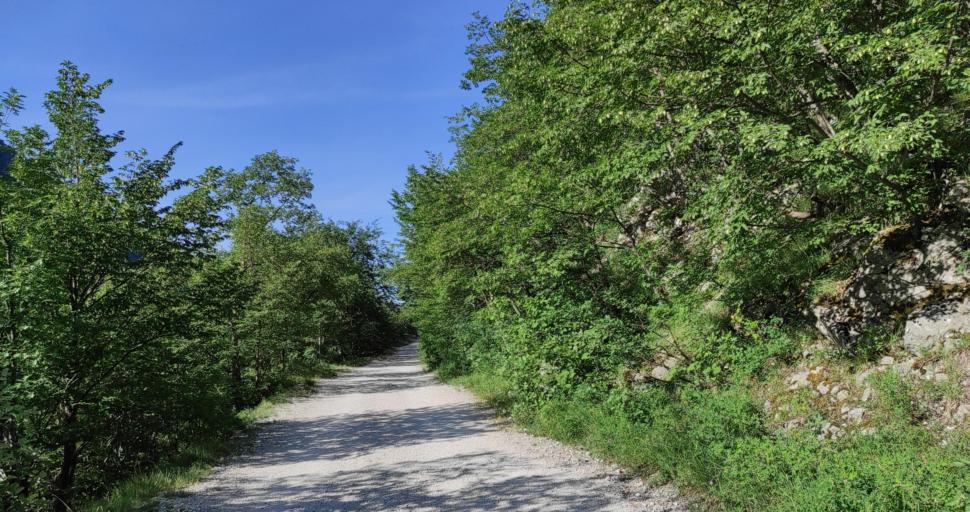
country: IT
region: The Marches
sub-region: Provincia di Ascoli Piceno
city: Montemonaco
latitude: 42.9256
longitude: 13.2827
